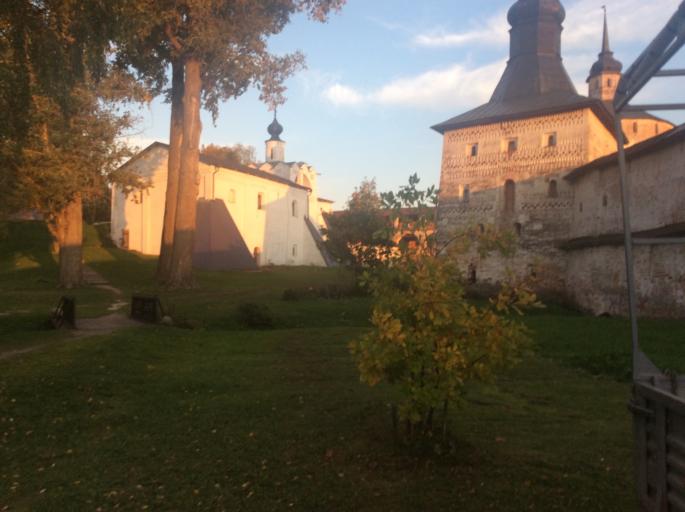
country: RU
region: Vologda
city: Kirillov
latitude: 59.8565
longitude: 38.3689
